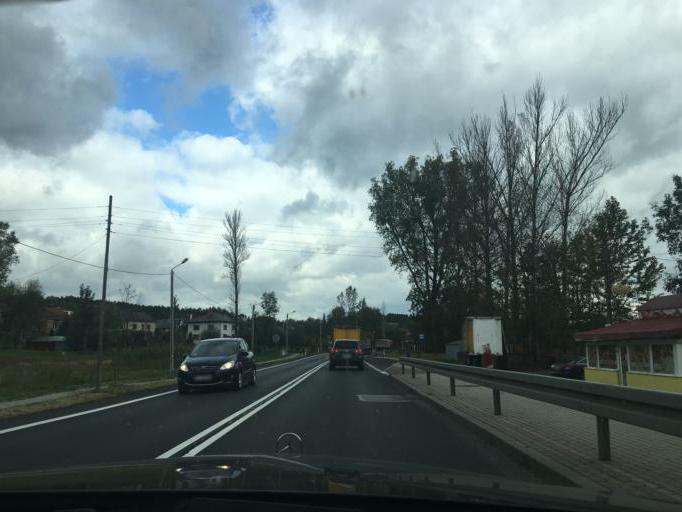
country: PL
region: Subcarpathian Voivodeship
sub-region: Powiat strzyzowski
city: Polomia
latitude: 49.9082
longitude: 21.8659
